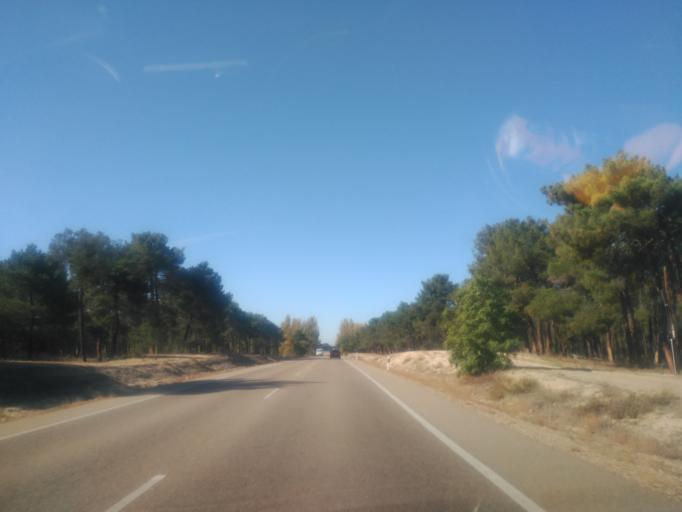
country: ES
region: Castille and Leon
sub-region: Provincia de Valladolid
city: Sardon de Duero
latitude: 41.6032
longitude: -4.4631
